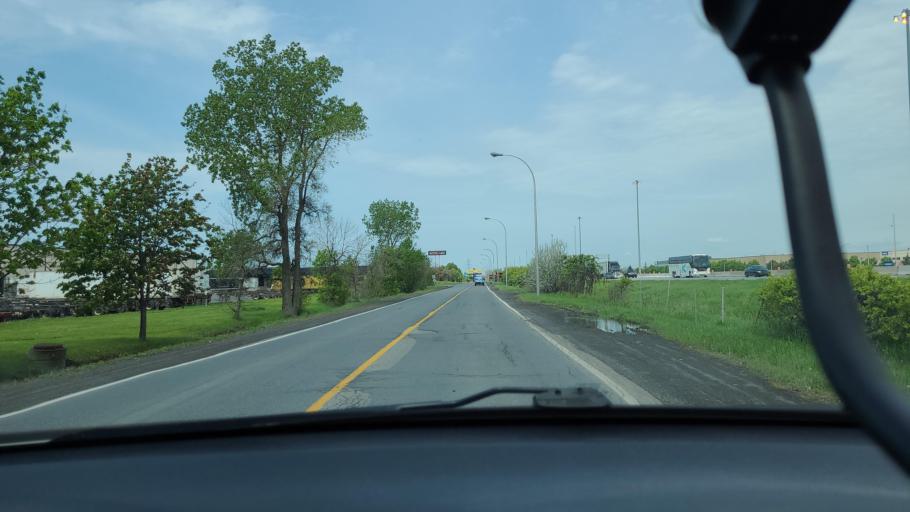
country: CA
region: Quebec
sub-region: Monteregie
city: Boucherville
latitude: 45.5687
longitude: -73.4320
